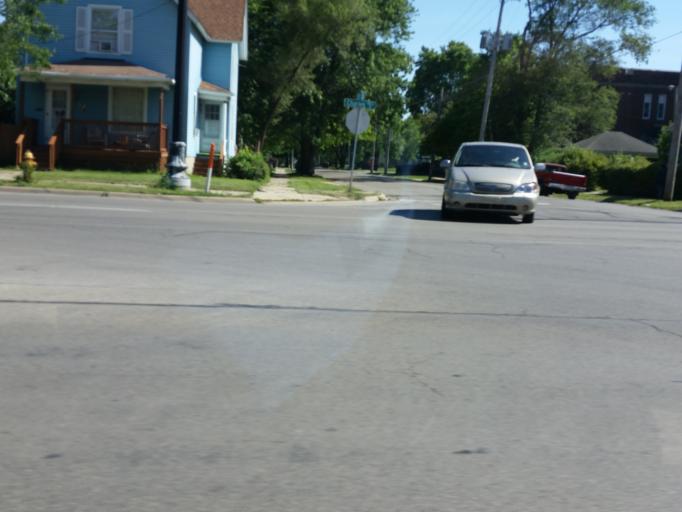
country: US
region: Illinois
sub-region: Winnebago County
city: Rockford
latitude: 42.2638
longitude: -89.0742
